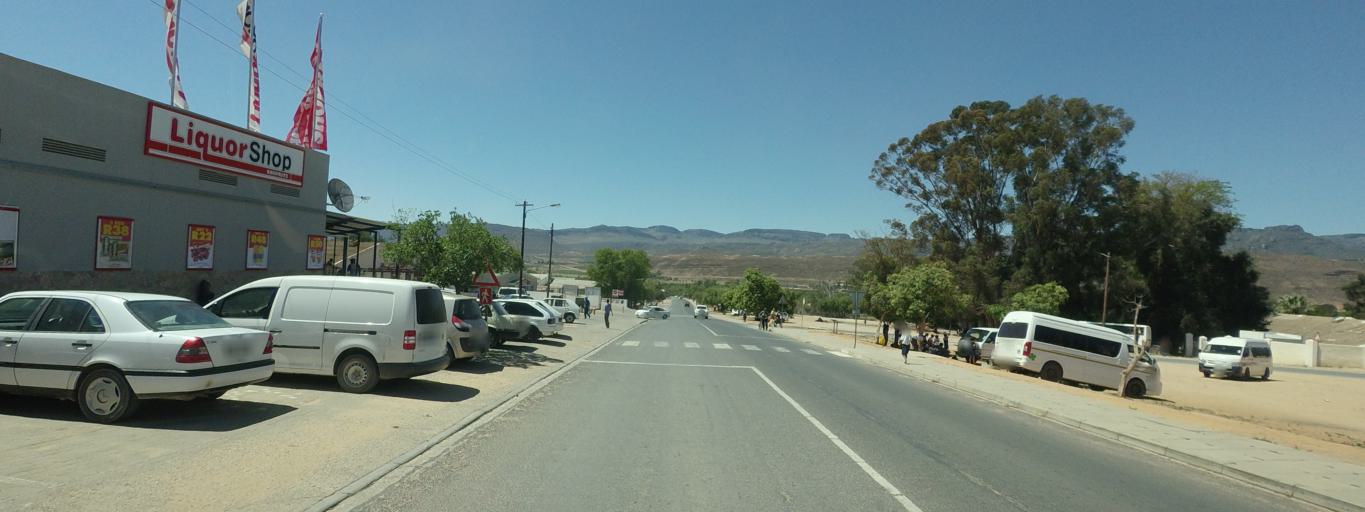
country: ZA
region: Western Cape
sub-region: West Coast District Municipality
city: Clanwilliam
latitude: -32.1871
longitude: 18.8903
